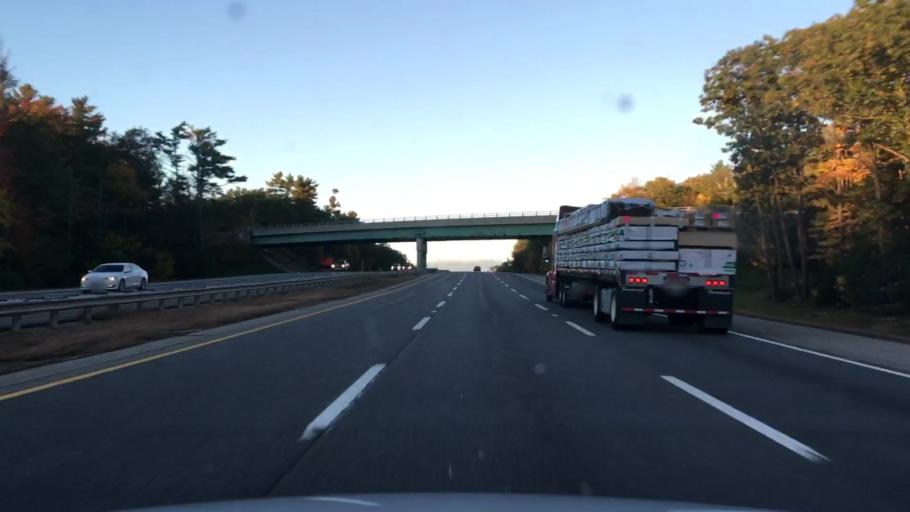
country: US
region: Maine
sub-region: York County
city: Wells Beach Station
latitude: 43.3561
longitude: -70.5898
